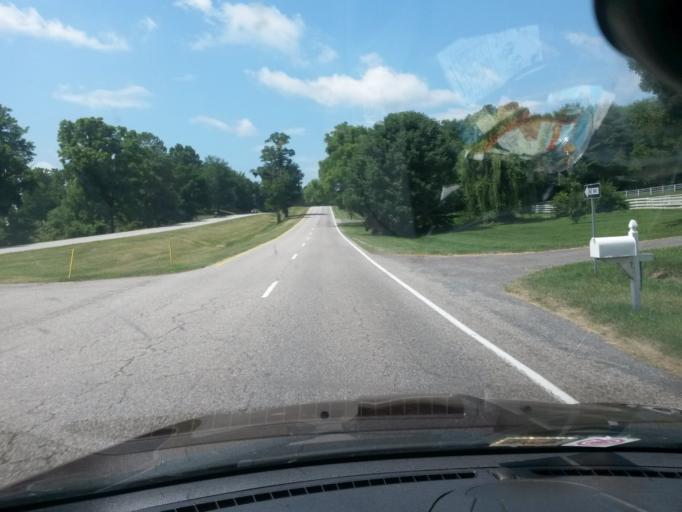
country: US
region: Virginia
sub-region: Rockbridge County
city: East Lexington
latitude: 37.8625
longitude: -79.3170
